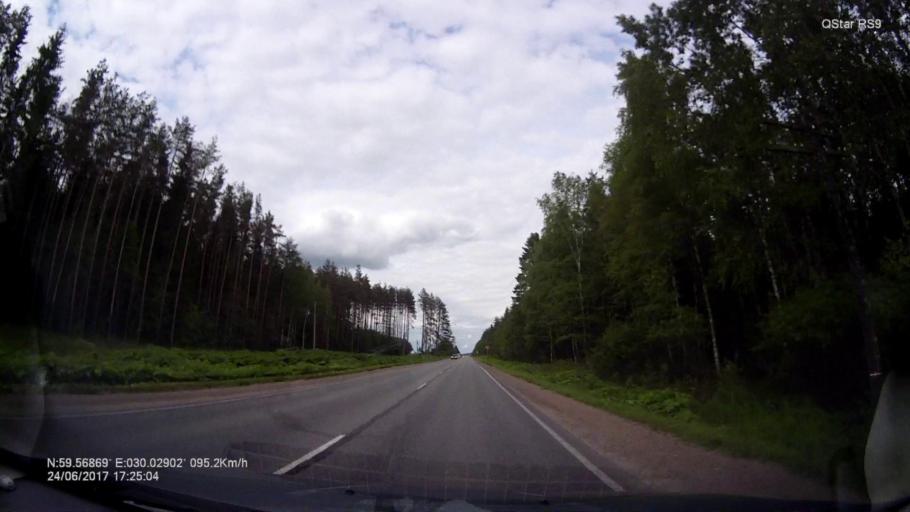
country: RU
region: Leningrad
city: Mariyenburg
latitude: 59.5689
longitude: 30.0295
